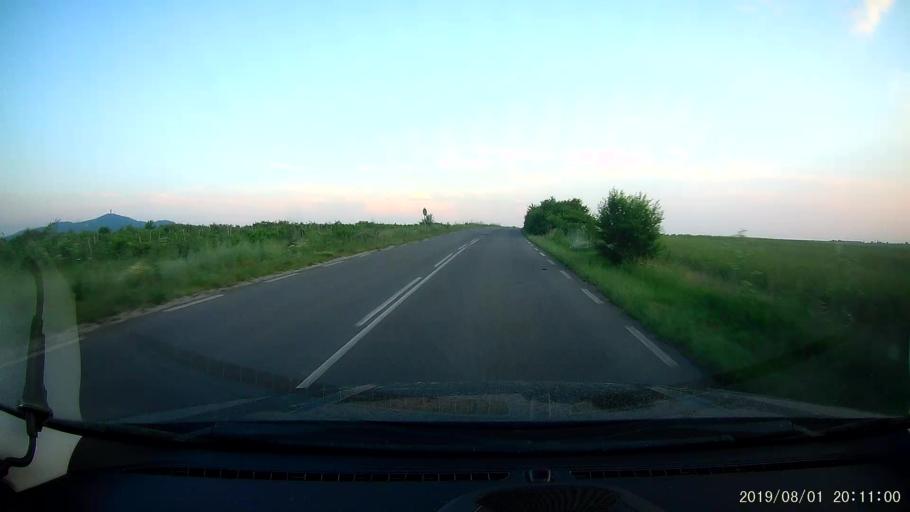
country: BG
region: Yambol
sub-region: Obshtina Yambol
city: Yambol
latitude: 42.4700
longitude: 26.6047
